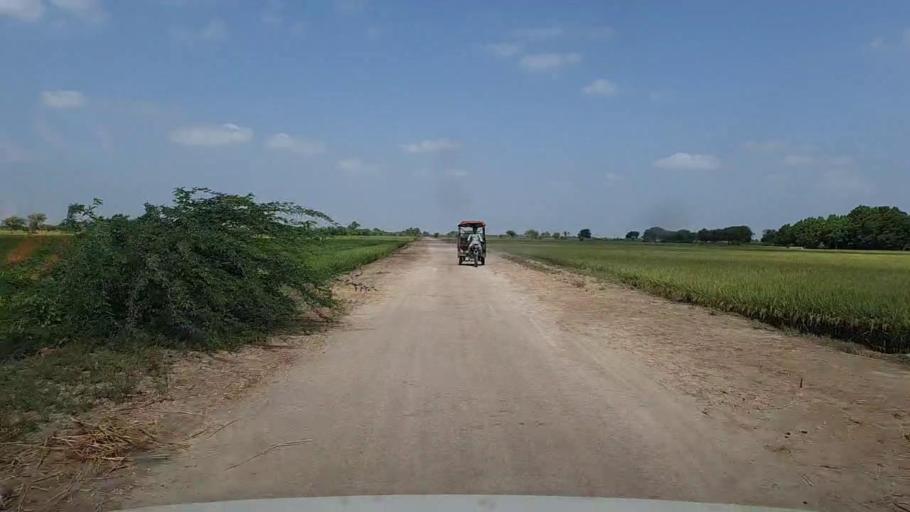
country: PK
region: Sindh
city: Kario
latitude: 24.6869
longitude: 68.5880
